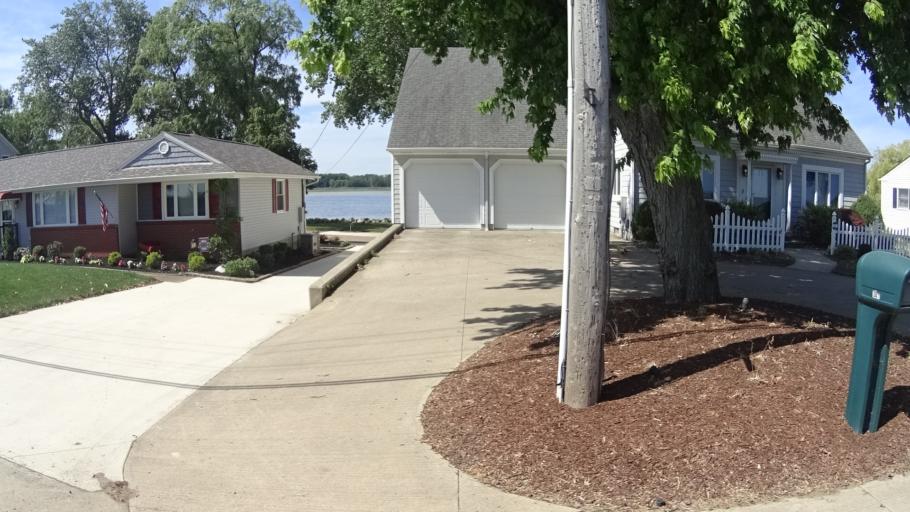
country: US
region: Ohio
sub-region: Erie County
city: Sandusky
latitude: 41.4369
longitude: -82.6266
